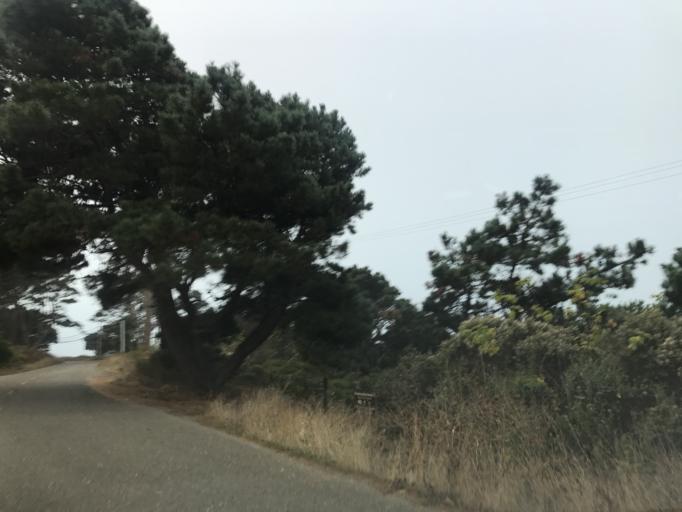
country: US
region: California
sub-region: Mendocino County
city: Fort Bragg
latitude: 39.2996
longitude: -123.7947
